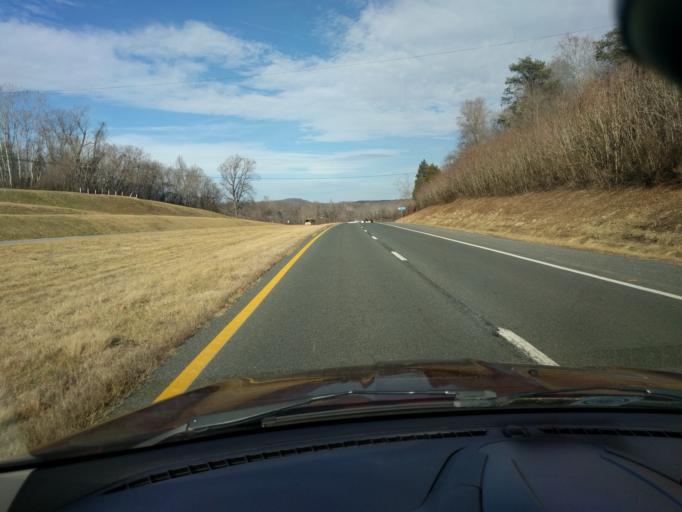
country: US
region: Virginia
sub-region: Amherst County
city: Madison Heights
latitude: 37.5030
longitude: -79.1234
